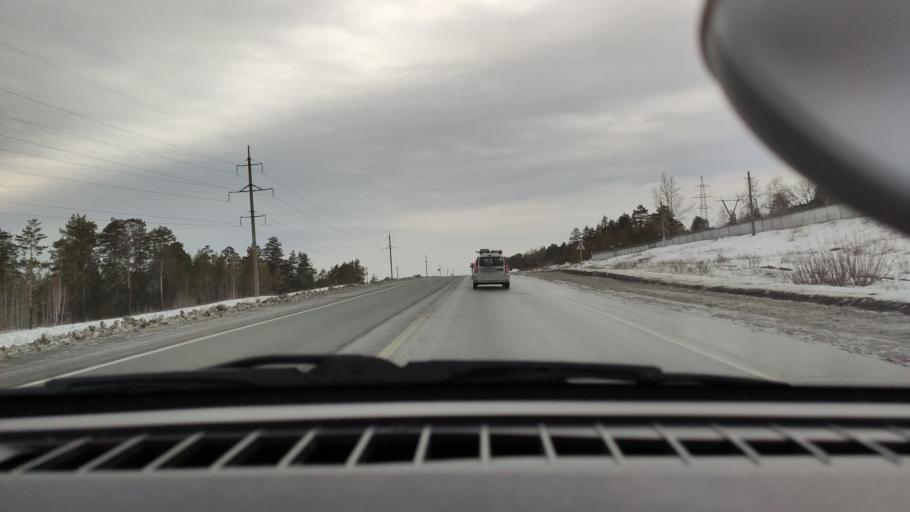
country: RU
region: Samara
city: Volzhskiy
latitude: 53.4561
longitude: 50.0863
